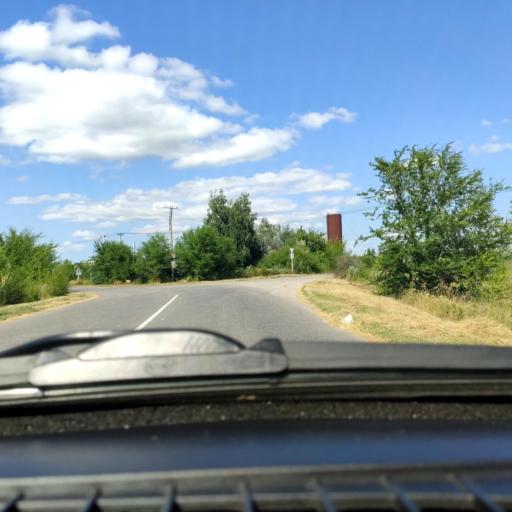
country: RU
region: Samara
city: Tol'yatti
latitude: 53.7198
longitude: 49.4246
